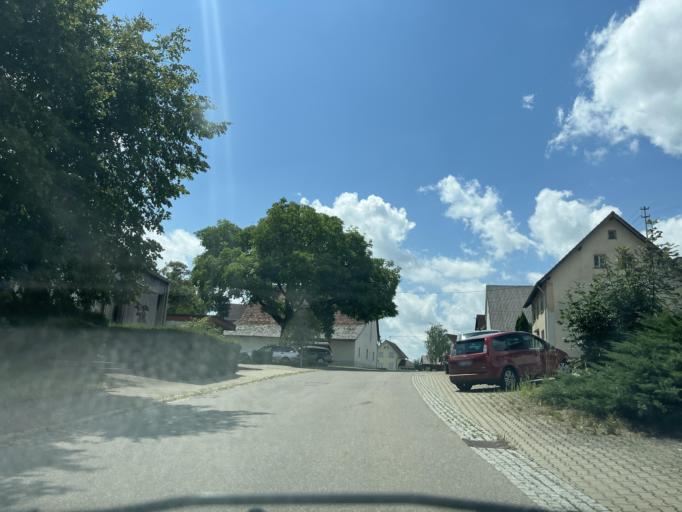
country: DE
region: Baden-Wuerttemberg
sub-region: Tuebingen Region
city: Leibertingen
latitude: 48.0087
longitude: 9.0389
